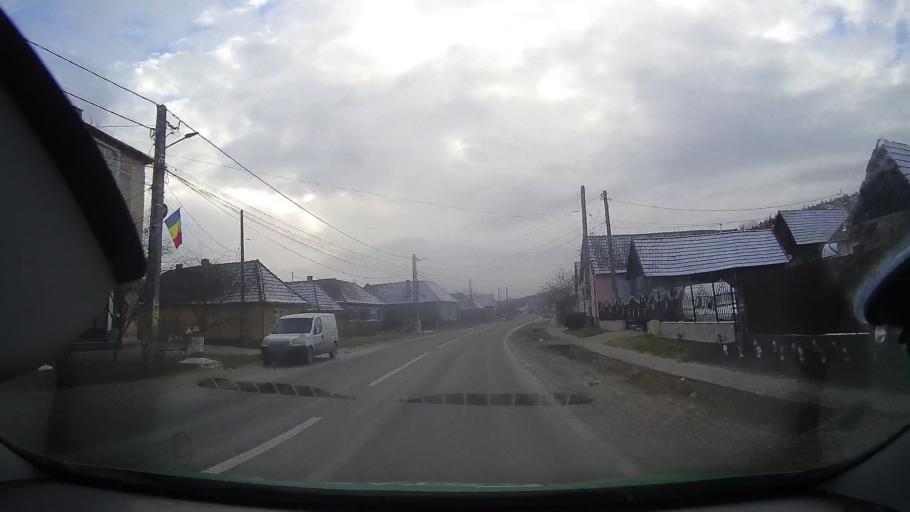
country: RO
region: Mures
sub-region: Comuna Cucerdea
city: Cucerdea
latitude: 46.4042
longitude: 24.2640
